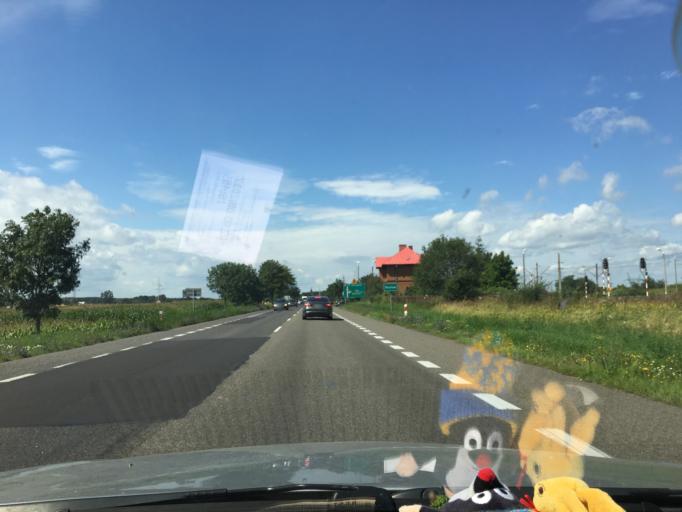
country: PL
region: West Pomeranian Voivodeship
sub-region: Powiat kamienski
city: Wolin
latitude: 53.8449
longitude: 14.6431
